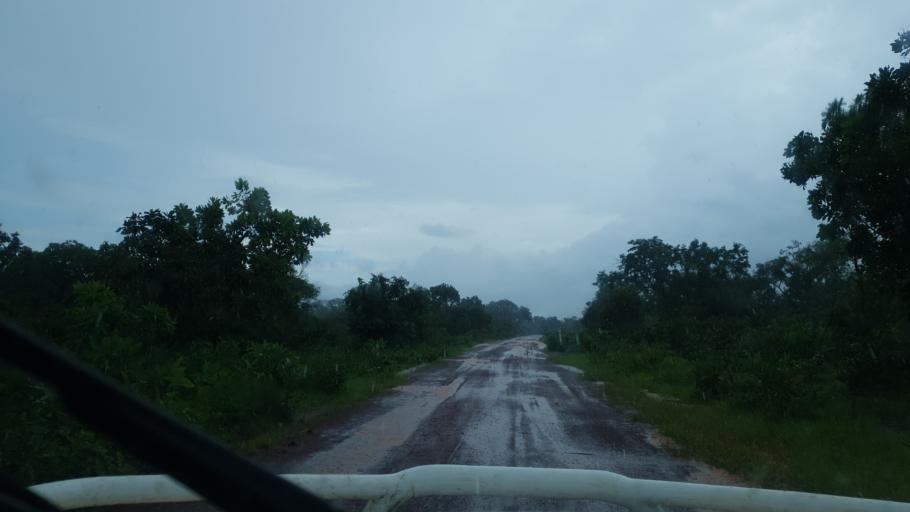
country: ML
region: Sikasso
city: Kolondieba
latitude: 11.6018
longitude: -6.6711
